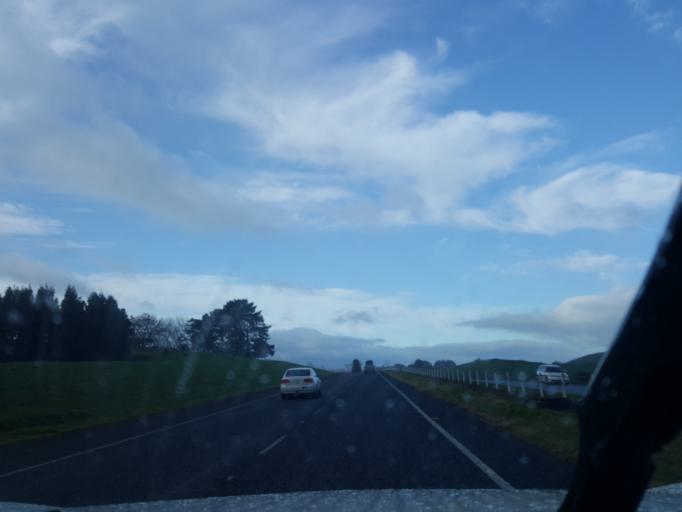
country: NZ
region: Waikato
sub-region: Waikato District
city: Ngaruawahia
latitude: -37.6641
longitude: 175.2067
